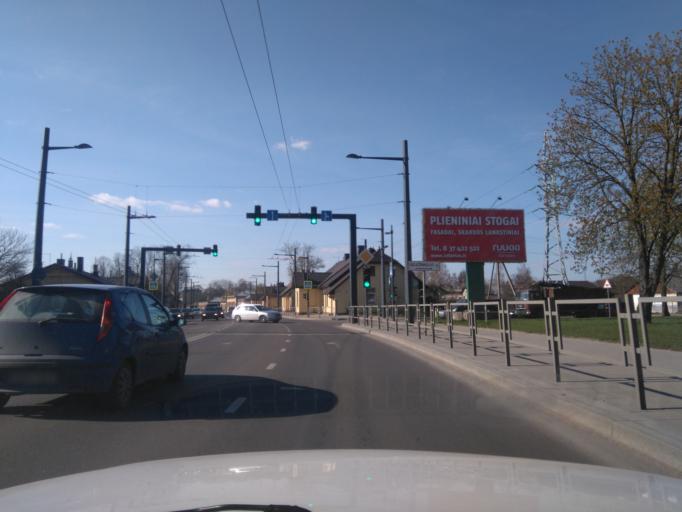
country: LT
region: Kauno apskritis
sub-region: Kaunas
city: Aleksotas
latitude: 54.8782
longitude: 23.9339
